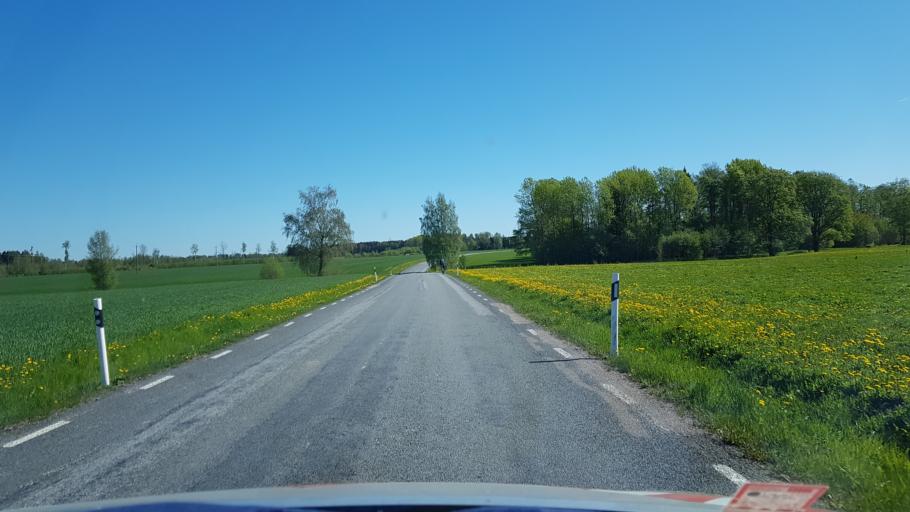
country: EE
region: Tartu
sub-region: Tartu linn
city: Tartu
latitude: 58.3981
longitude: 26.8649
